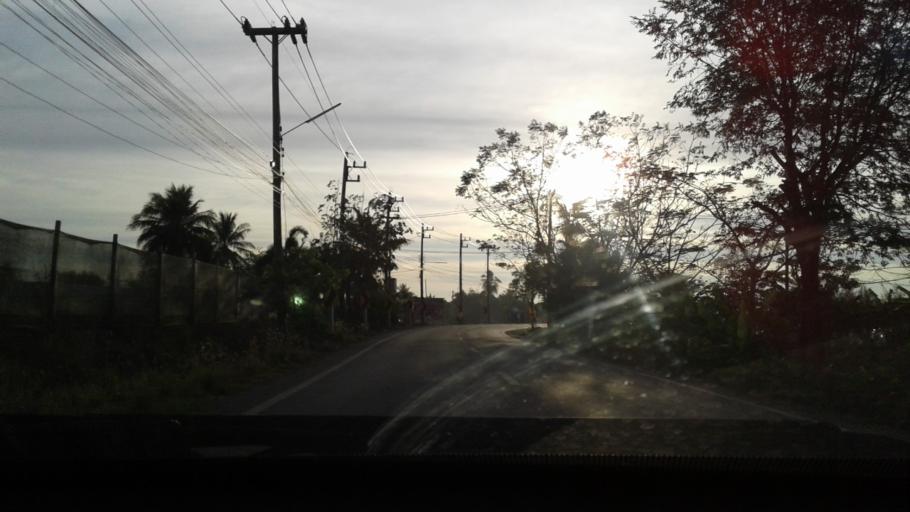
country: TH
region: Nakhon Pathom
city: Nakhon Chai Si
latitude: 13.8977
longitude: 100.2362
